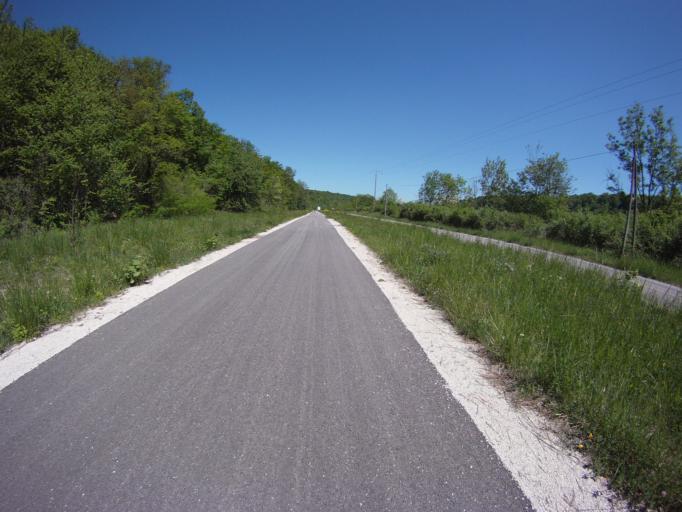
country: FR
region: Lorraine
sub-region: Departement de Meurthe-et-Moselle
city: Villey-Saint-Etienne
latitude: 48.7458
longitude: 6.0045
